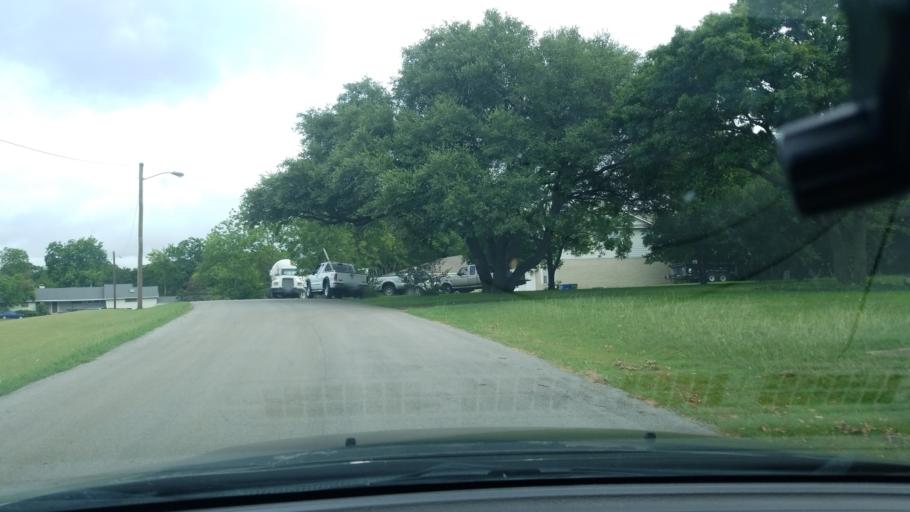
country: US
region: Texas
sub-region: Dallas County
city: Highland Park
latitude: 32.8162
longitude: -96.6938
